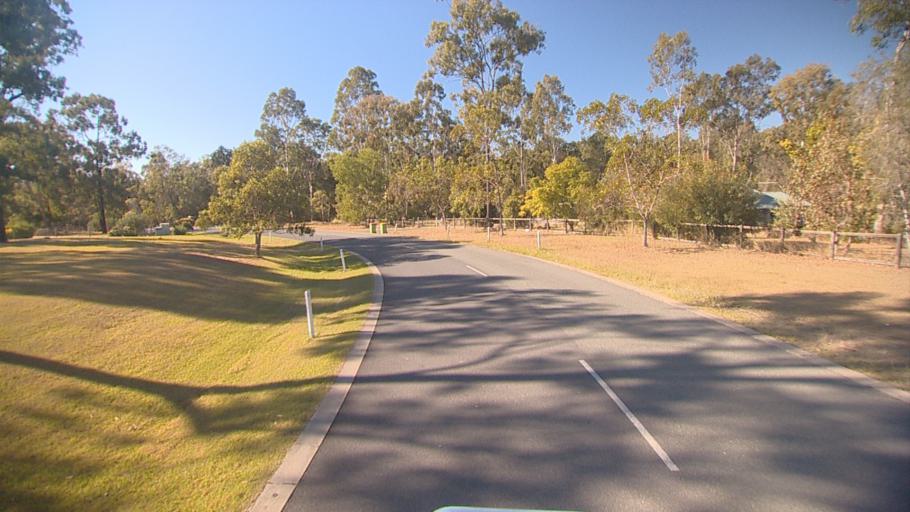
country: AU
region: Queensland
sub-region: Logan
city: North Maclean
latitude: -27.7577
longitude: 152.9586
